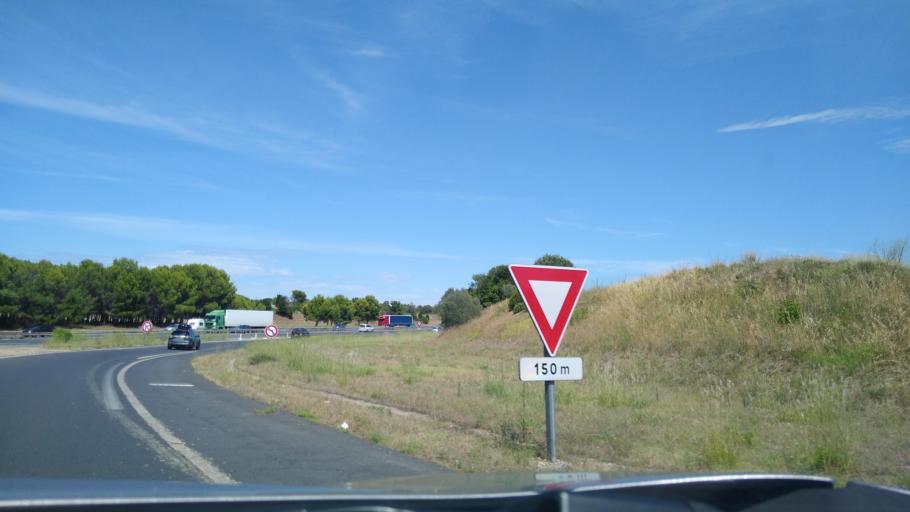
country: FR
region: Languedoc-Roussillon
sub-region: Departement de l'Herault
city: Poussan
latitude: 43.4807
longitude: 3.6842
